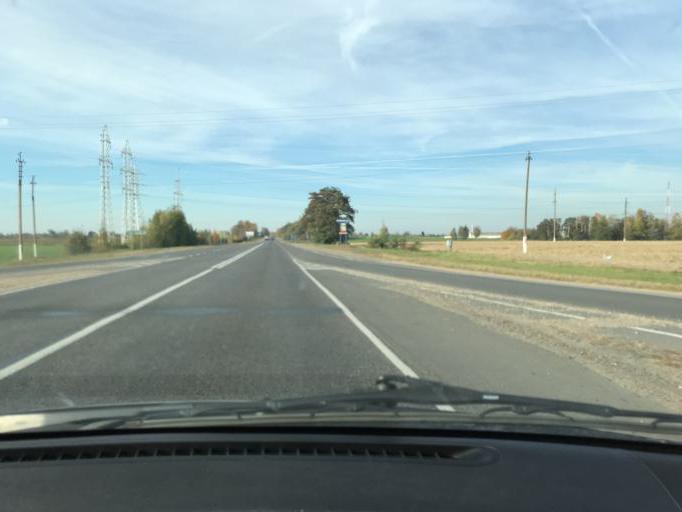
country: BY
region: Brest
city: Asnyezhytsy
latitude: 52.1866
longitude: 26.0782
